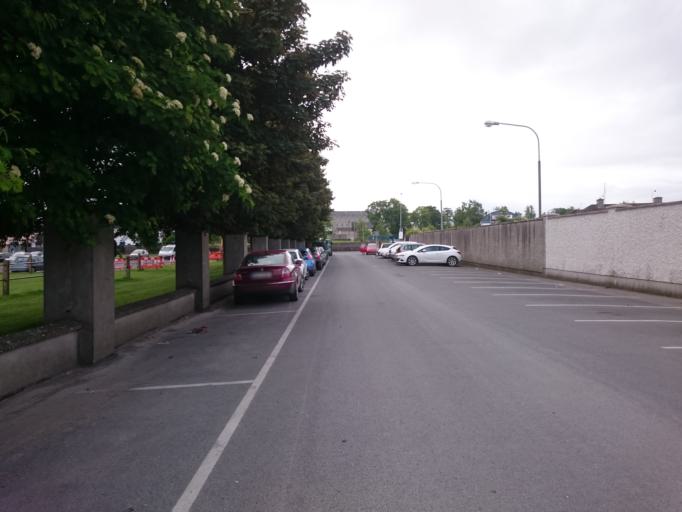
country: IE
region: Leinster
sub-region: Kilkenny
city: Kilkenny
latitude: 52.6501
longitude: -7.2585
